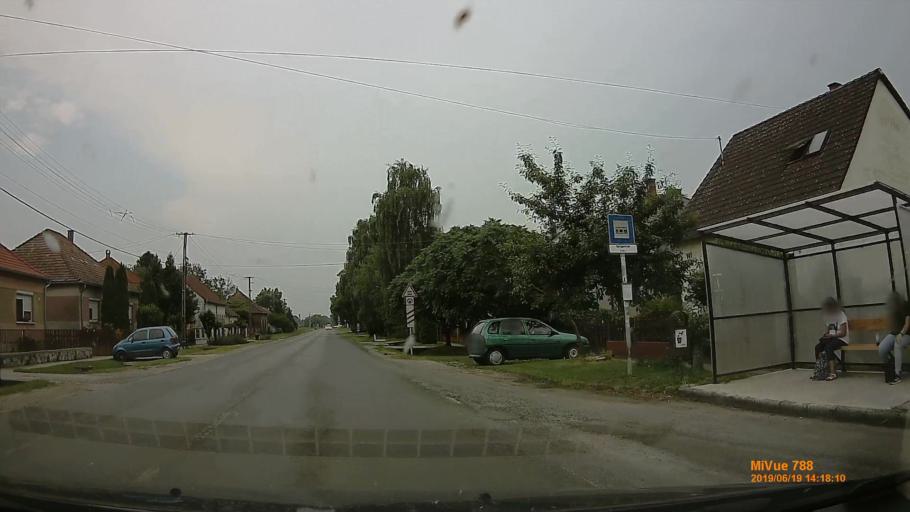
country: HU
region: Baranya
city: Szigetvar
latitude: 46.0447
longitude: 17.7817
